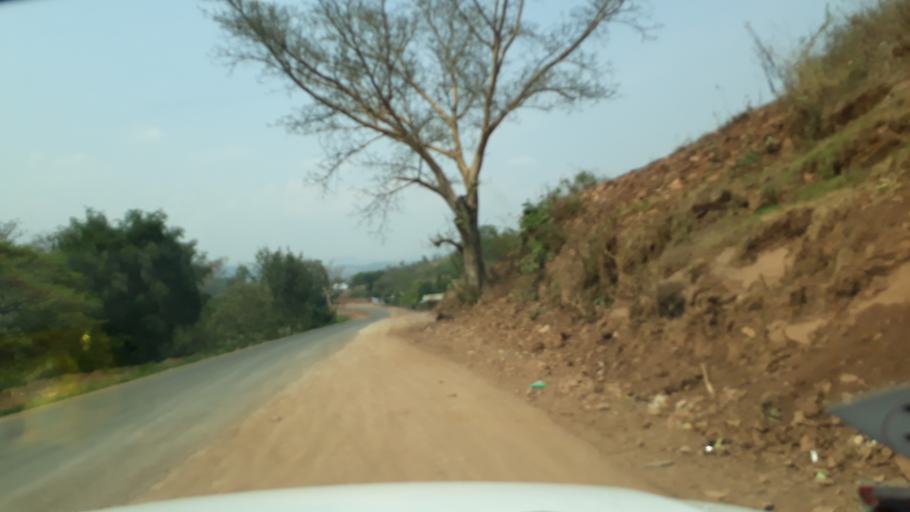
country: ET
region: Oromiya
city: Agaro
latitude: 7.9074
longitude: 36.5544
